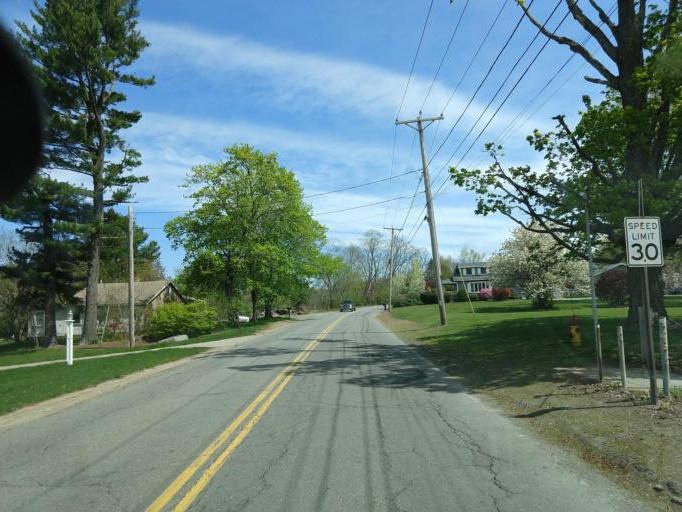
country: US
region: Massachusetts
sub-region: Essex County
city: Amesbury
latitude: 42.8606
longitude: -70.9048
